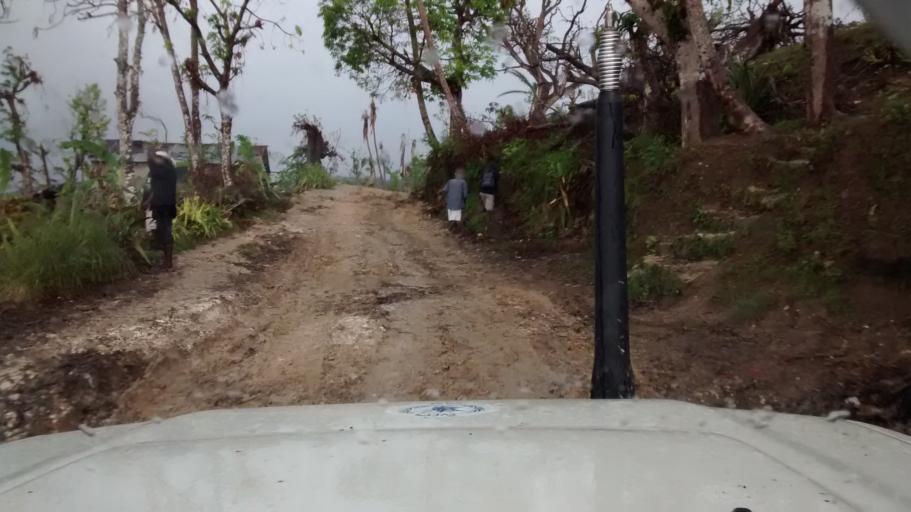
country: HT
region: Grandans
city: Moron
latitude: 18.5383
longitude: -74.1573
